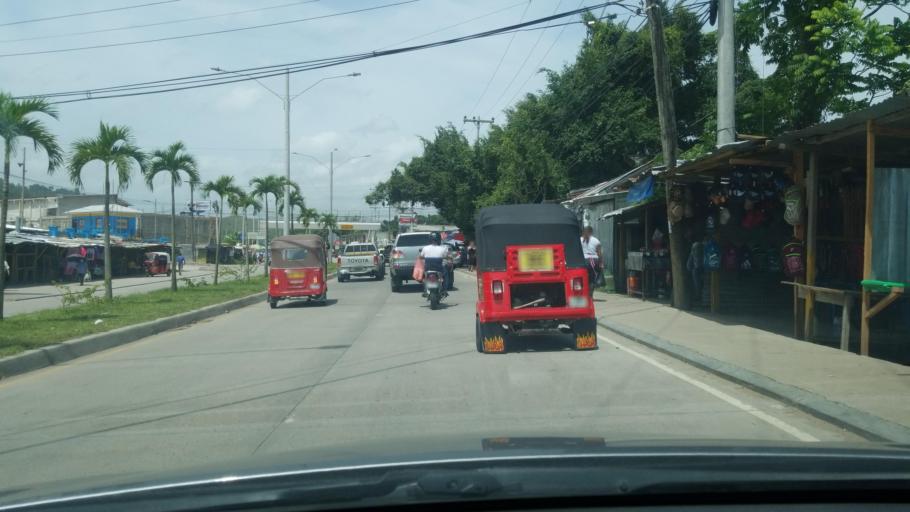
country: HN
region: Copan
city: La Entrada
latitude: 15.0593
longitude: -88.7536
